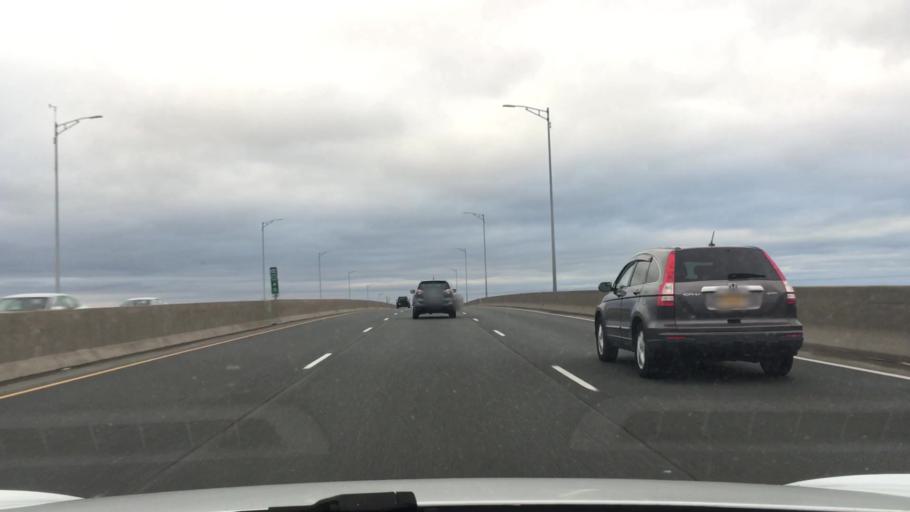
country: CA
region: Ontario
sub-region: Regional Municipality of Niagara
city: St. Catharines
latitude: 43.1677
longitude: -79.1959
